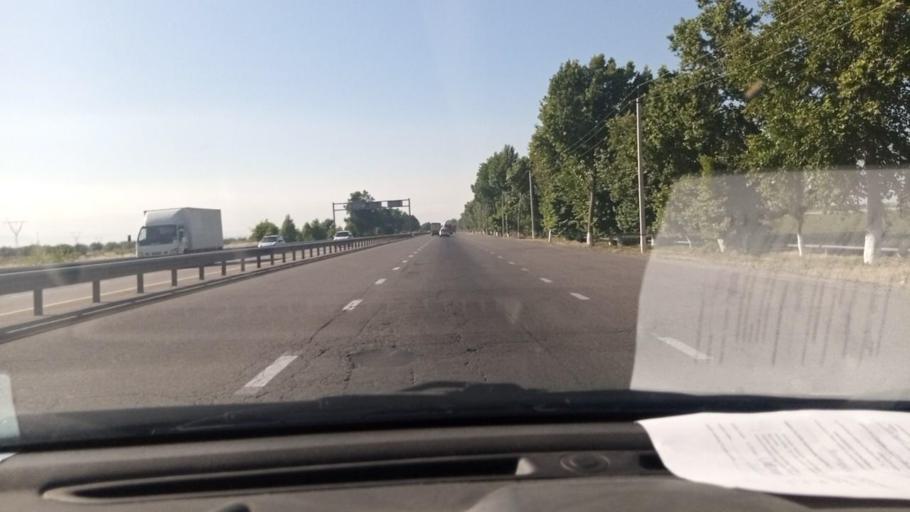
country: UZ
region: Toshkent Shahri
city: Bektemir
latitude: 41.1804
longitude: 69.4073
